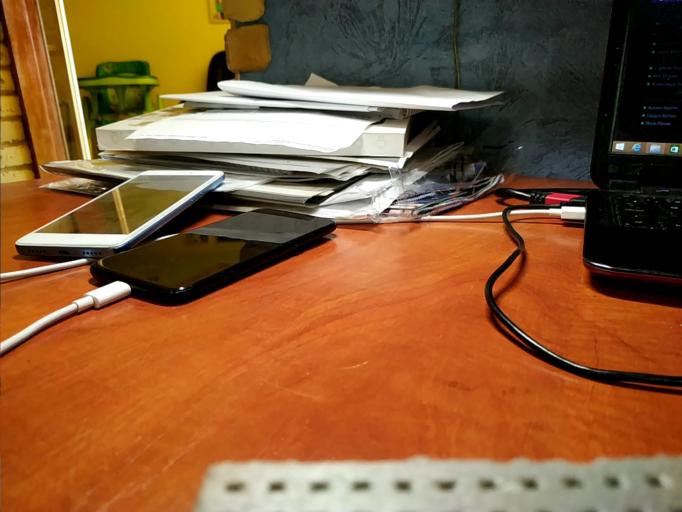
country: RU
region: Tverskaya
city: Spirovo
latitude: 57.4172
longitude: 35.1279
